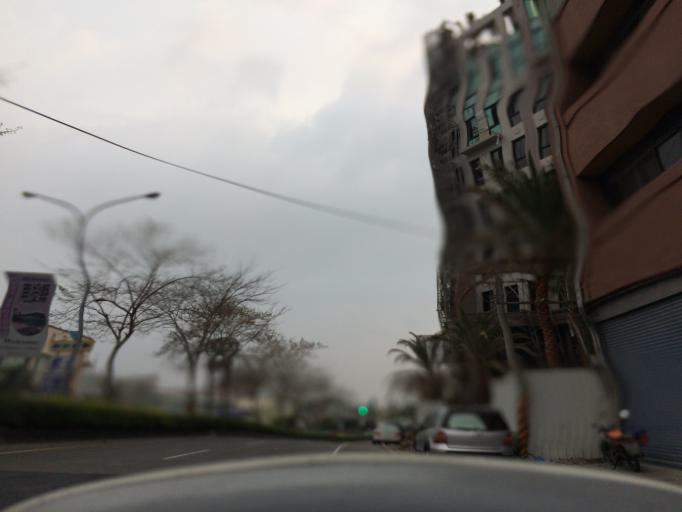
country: TW
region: Taiwan
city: Zhongxing New Village
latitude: 24.0041
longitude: 120.6942
